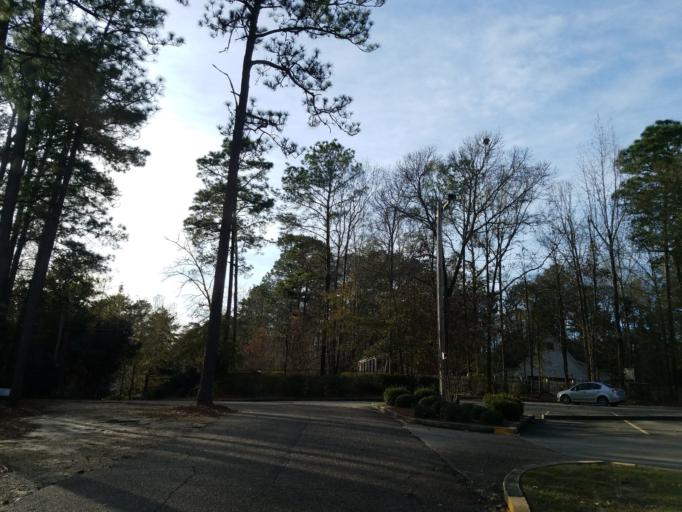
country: US
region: Mississippi
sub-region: Lamar County
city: West Hattiesburg
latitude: 31.3061
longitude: -89.3454
